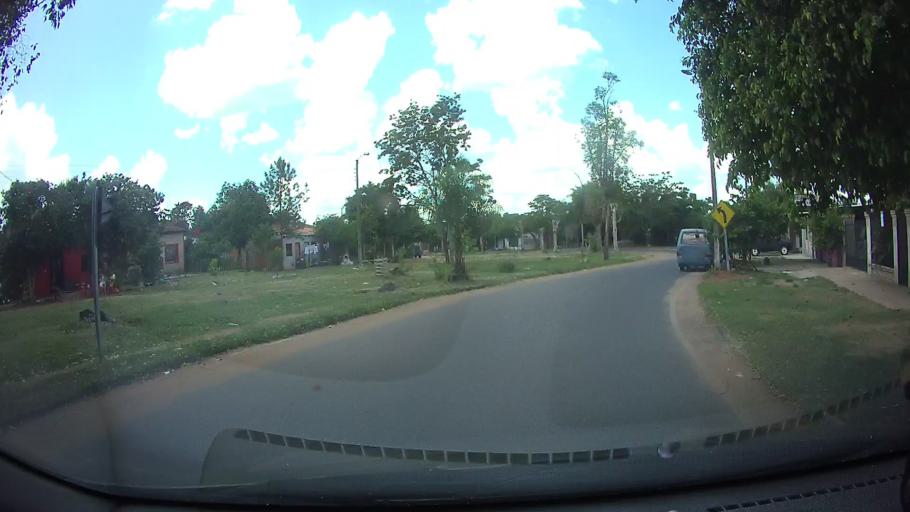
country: PY
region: Central
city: Limpio
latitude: -25.1661
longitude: -57.4323
